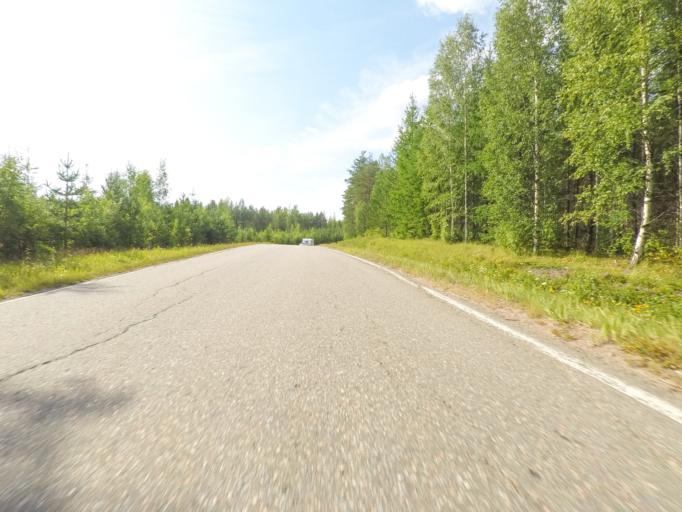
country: FI
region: Southern Savonia
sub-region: Mikkeli
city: Puumala
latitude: 61.6883
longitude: 28.2217
